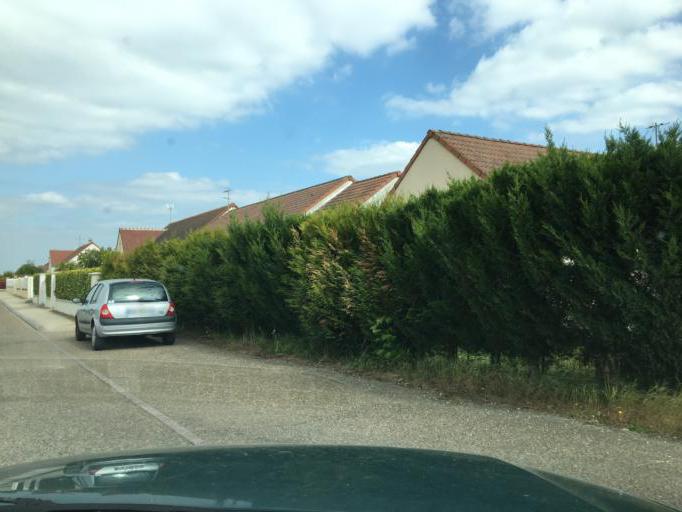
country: FR
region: Centre
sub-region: Departement du Loiret
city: Beaugency
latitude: 47.7872
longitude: 1.6212
